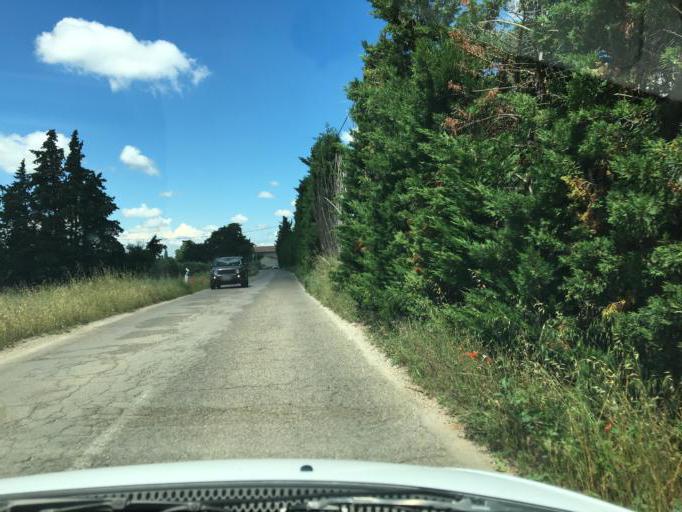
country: FR
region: Provence-Alpes-Cote d'Azur
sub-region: Departement du Vaucluse
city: Carpentras
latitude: 44.0364
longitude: 5.0570
